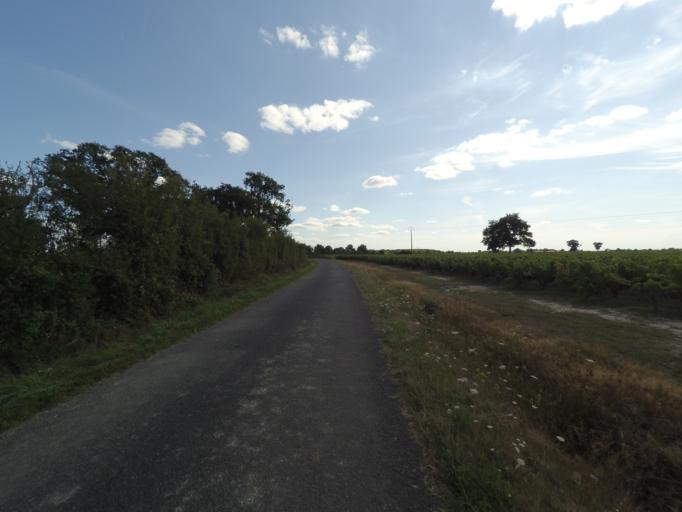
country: FR
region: Pays de la Loire
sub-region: Departement de la Loire-Atlantique
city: Vieillevigne
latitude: 46.9606
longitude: -1.4428
